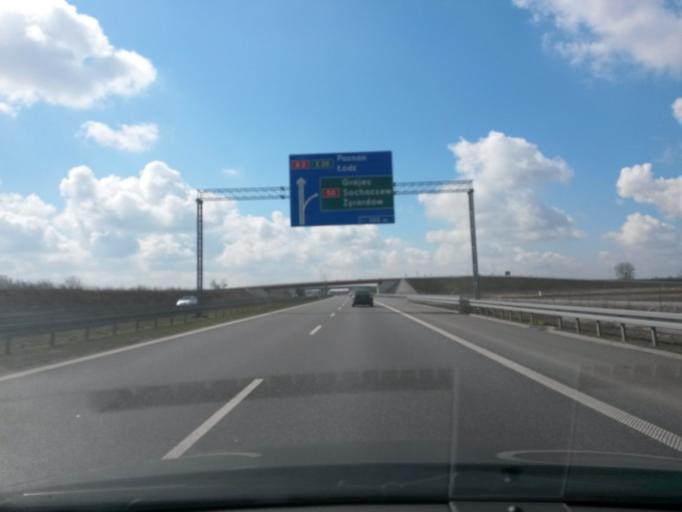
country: PL
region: Masovian Voivodeship
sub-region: Powiat zyrardowski
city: Wiskitki
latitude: 52.0919
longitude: 20.3713
